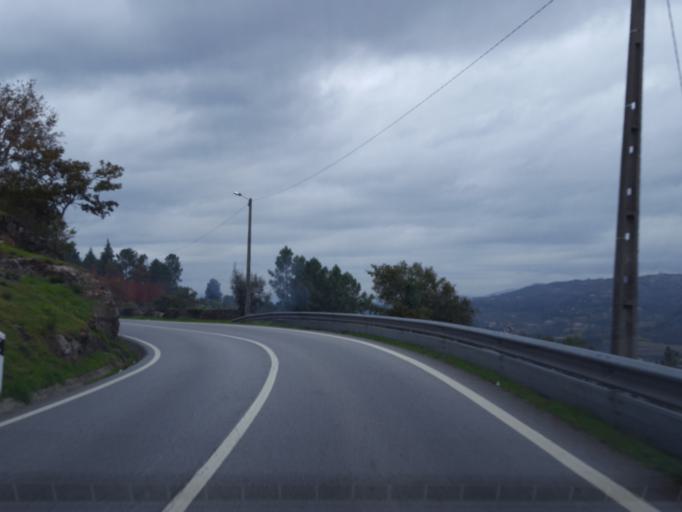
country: PT
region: Porto
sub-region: Marco de Canaveses
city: Marco de Canavezes
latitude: 41.1633
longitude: -8.1457
